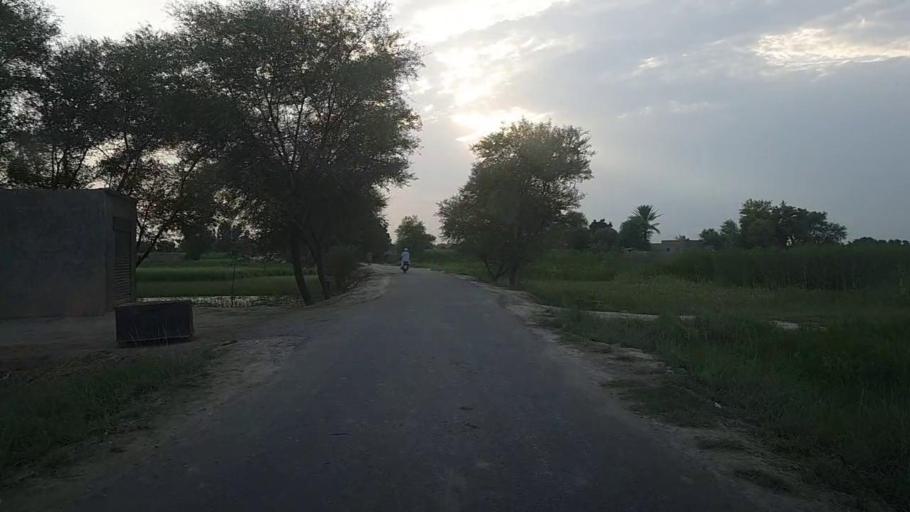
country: PK
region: Sindh
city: Ubauro
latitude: 28.3539
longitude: 69.7799
